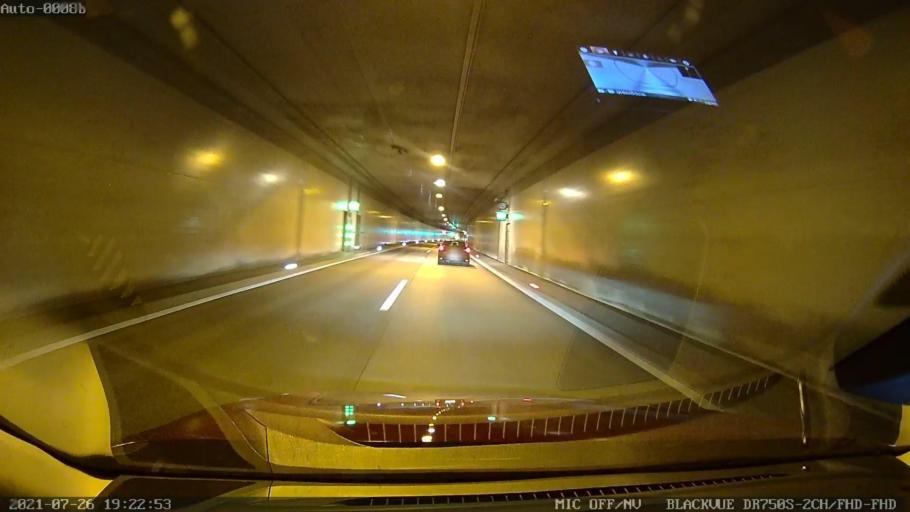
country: AT
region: Upper Austria
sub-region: Politischer Bezirk Kirchdorf an der Krems
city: Micheldorf in Oberoesterreich
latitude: 47.8855
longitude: 14.1085
